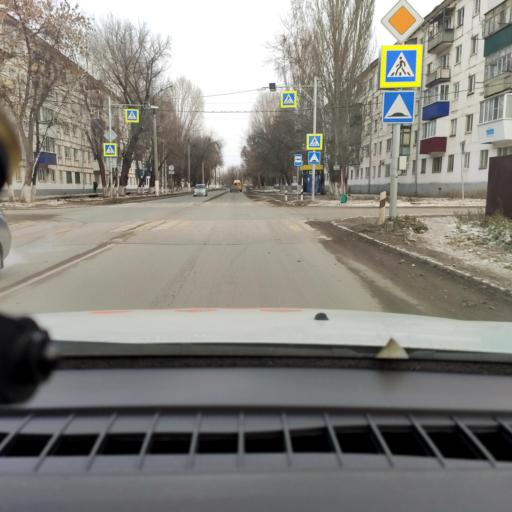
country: RU
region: Samara
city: Chapayevsk
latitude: 52.9623
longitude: 49.6891
